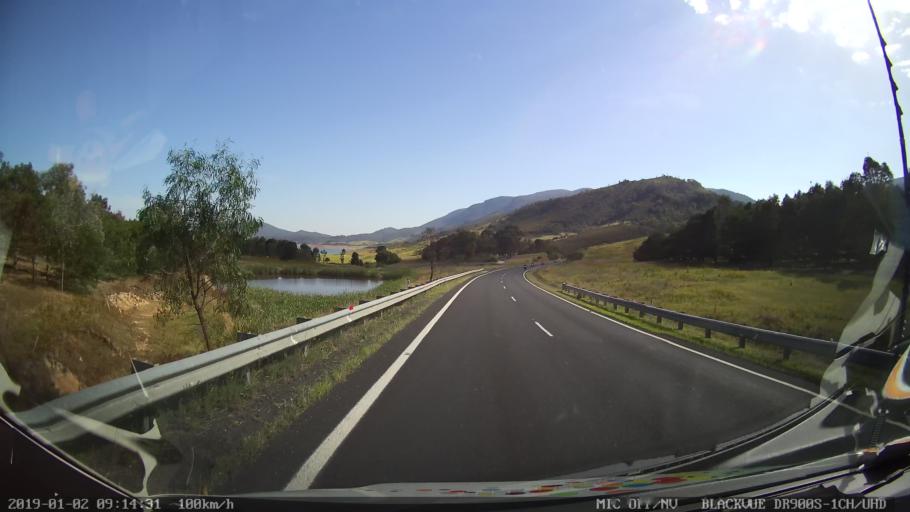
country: AU
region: New South Wales
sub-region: Tumut Shire
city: Tumut
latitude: -35.4762
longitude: 148.2746
